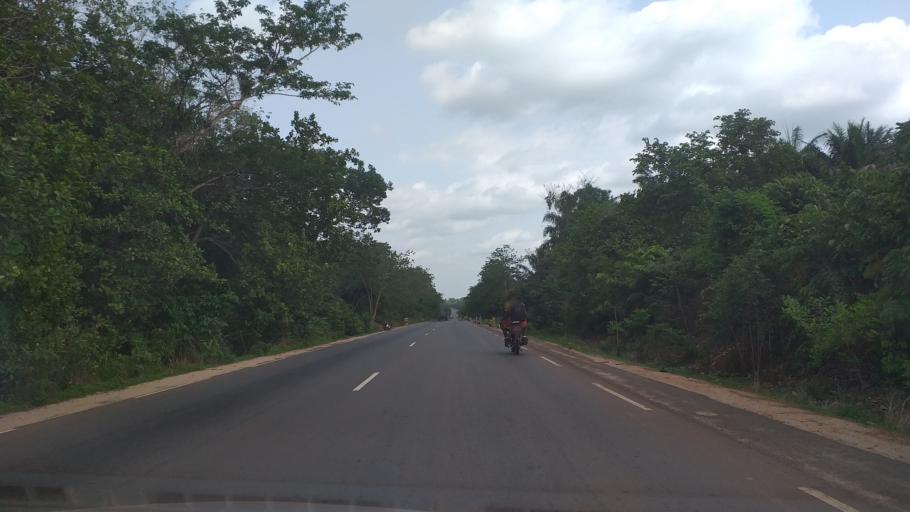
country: GN
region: Boke
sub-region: Boke Prefecture
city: Sangueya
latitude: 10.7438
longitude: -14.3794
